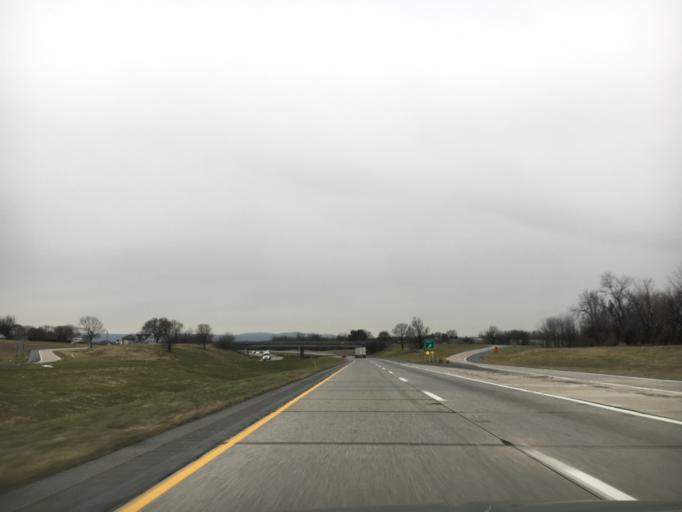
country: US
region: Pennsylvania
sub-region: Berks County
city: Kutztown
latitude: 40.5071
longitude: -75.8026
